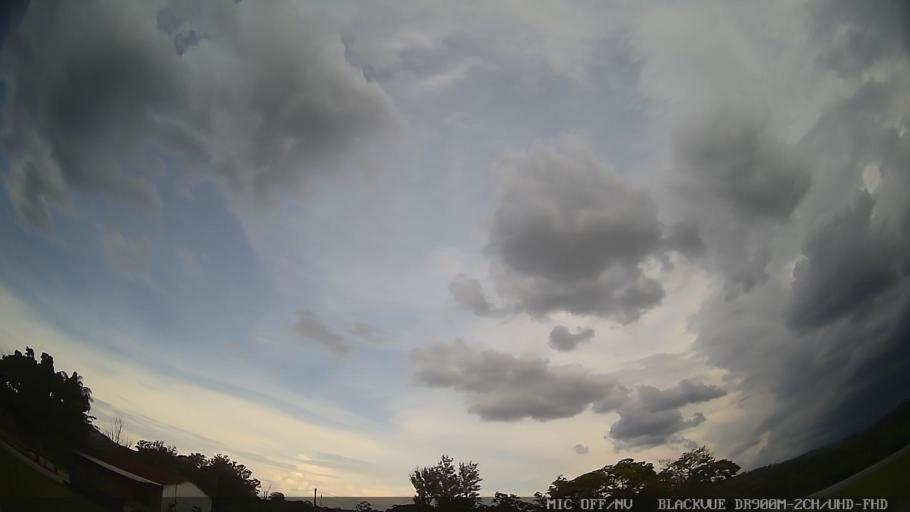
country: BR
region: Sao Paulo
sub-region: Amparo
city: Amparo
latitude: -22.8532
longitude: -46.7843
